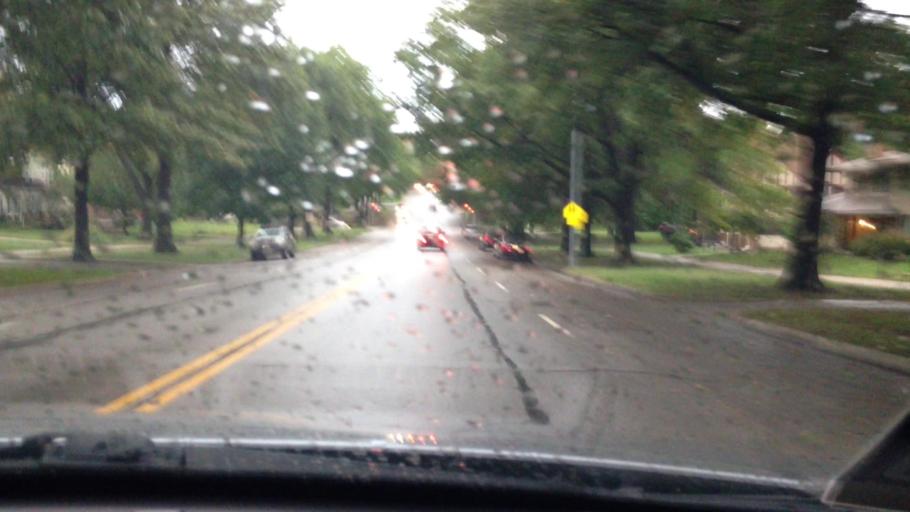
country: US
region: Kansas
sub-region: Johnson County
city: Mission Hills
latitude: 39.0118
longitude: -94.5820
